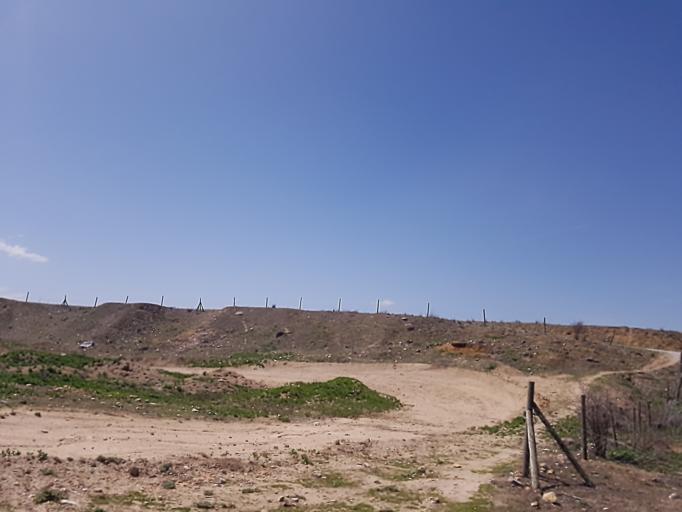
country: ES
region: Castille and Leon
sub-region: Provincia de Segovia
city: Segovia
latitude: 40.9464
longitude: -4.1304
